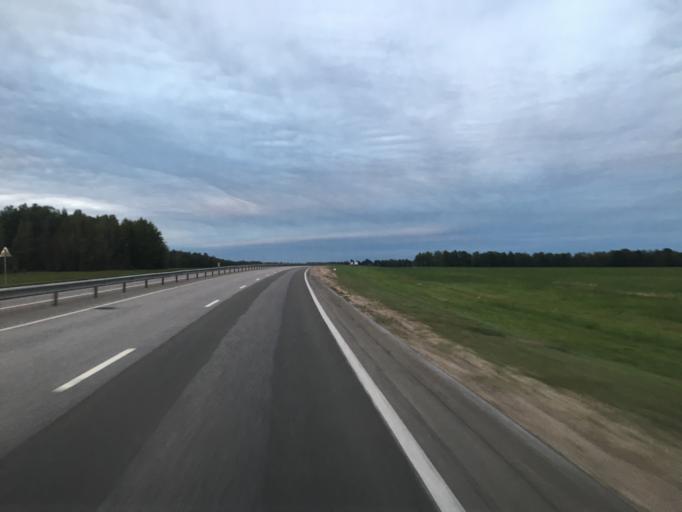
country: RU
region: Kaluga
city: Kaluga
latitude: 54.6673
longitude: 36.2862
